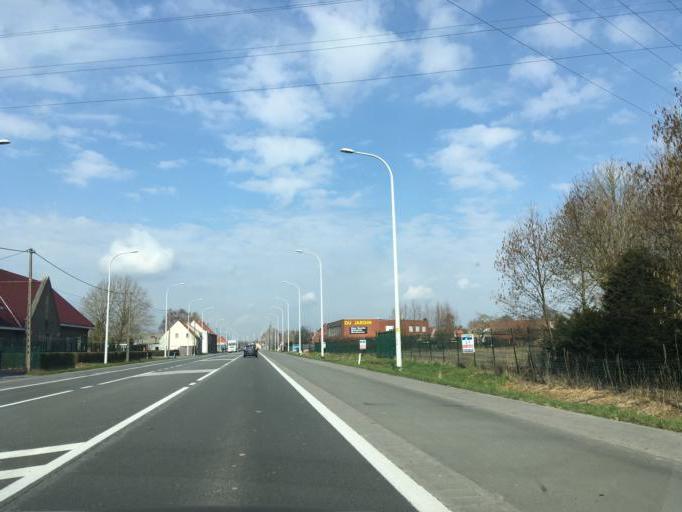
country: BE
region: Flanders
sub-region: Provincie West-Vlaanderen
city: Lendelede
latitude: 50.8986
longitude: 3.2287
